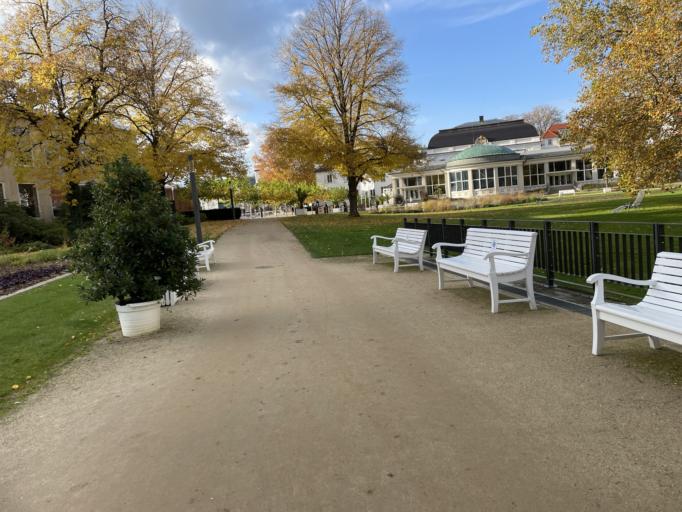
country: DE
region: North Rhine-Westphalia
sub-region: Regierungsbezirk Detmold
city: Bad Salzuflen
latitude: 52.0874
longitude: 8.7503
